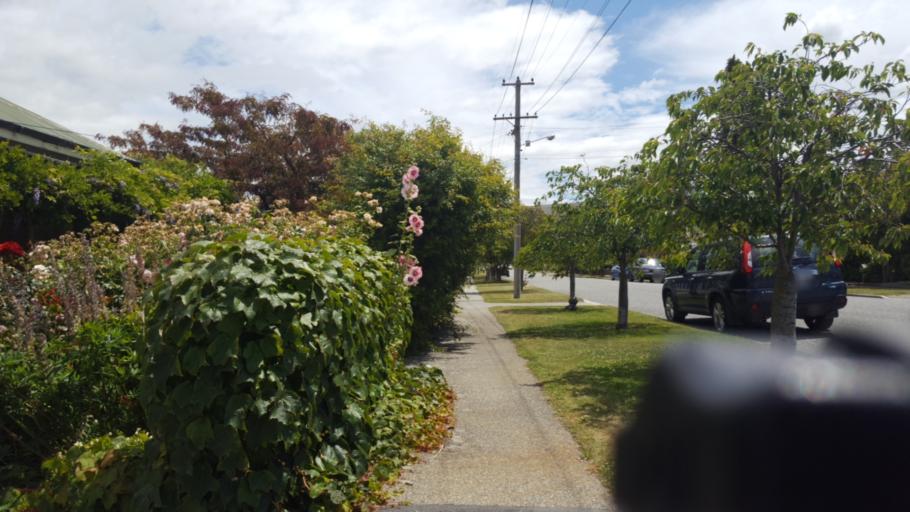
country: NZ
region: Otago
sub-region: Queenstown-Lakes District
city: Wanaka
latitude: -45.0445
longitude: 169.2099
